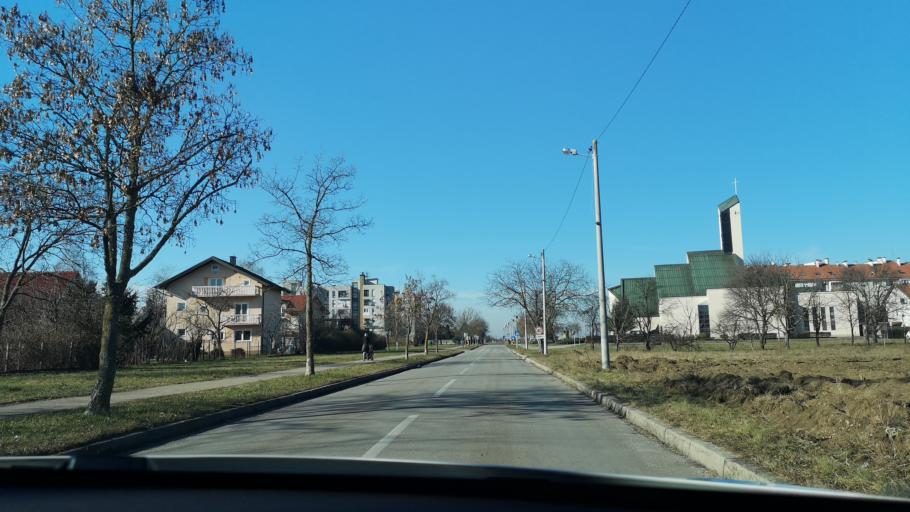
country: HR
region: Zagrebacka
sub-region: Grad Velika Gorica
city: Velika Gorica
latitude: 45.7214
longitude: 16.0658
